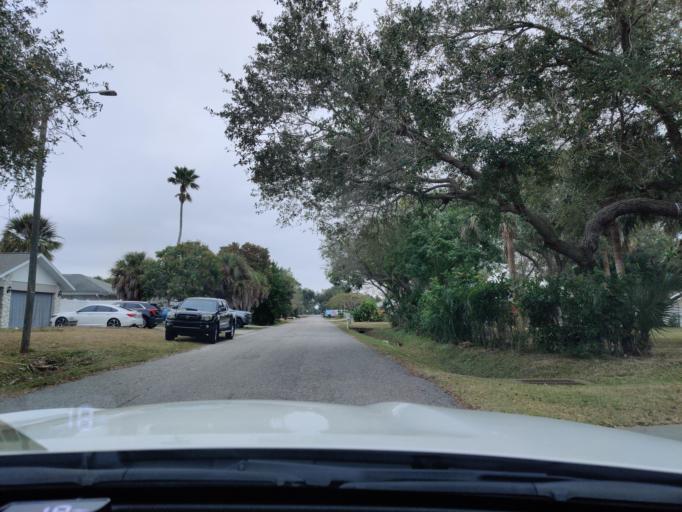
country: US
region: Florida
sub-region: Sarasota County
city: South Venice
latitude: 27.0387
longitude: -82.4096
